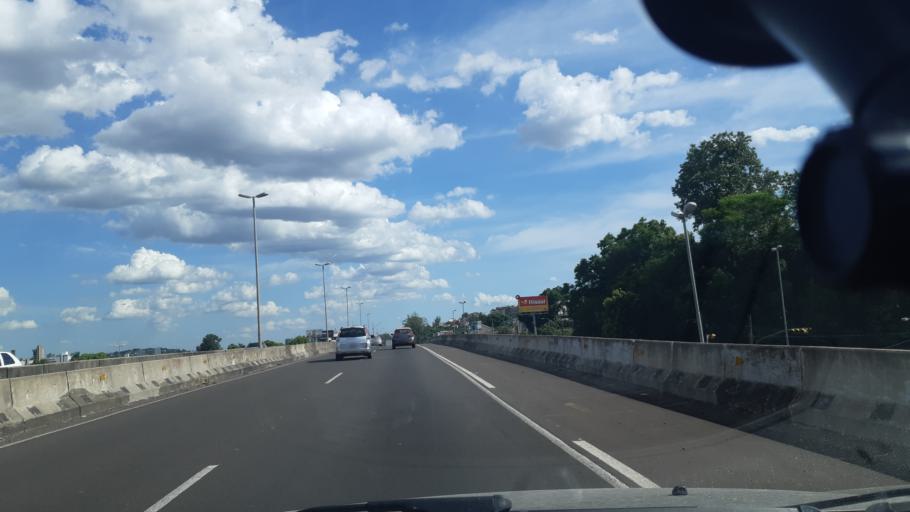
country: BR
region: Rio Grande do Sul
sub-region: Novo Hamburgo
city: Novo Hamburgo
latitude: -29.6694
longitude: -51.1432
